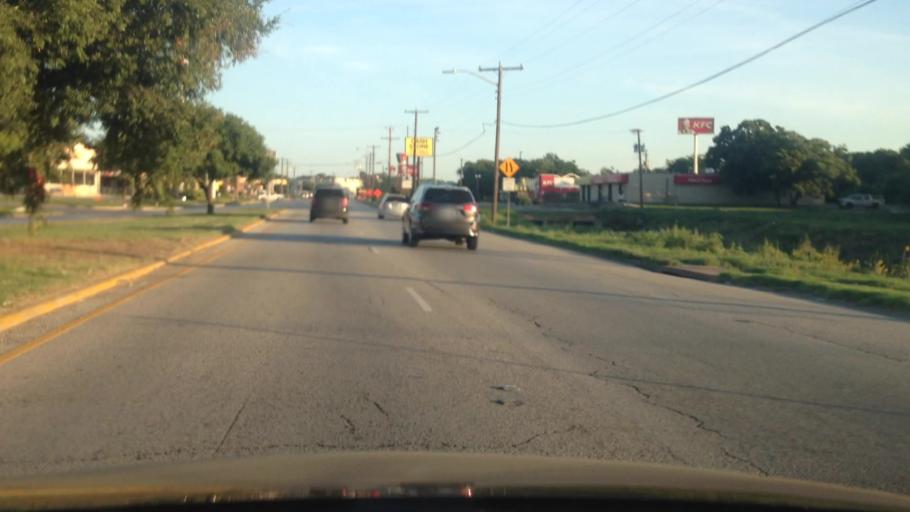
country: US
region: Texas
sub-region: Tarrant County
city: Haltom City
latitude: 32.7755
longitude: -97.2881
